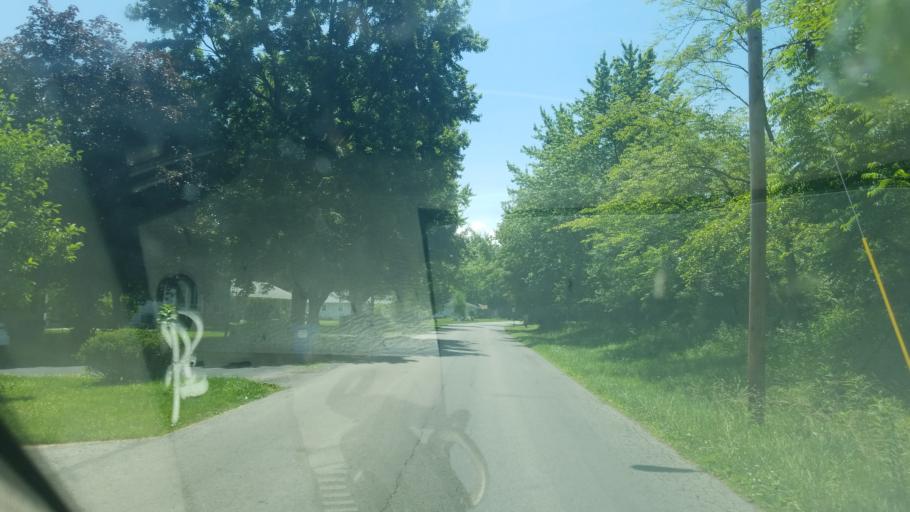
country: US
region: Ohio
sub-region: Hancock County
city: Findlay
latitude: 41.0206
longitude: -83.6347
